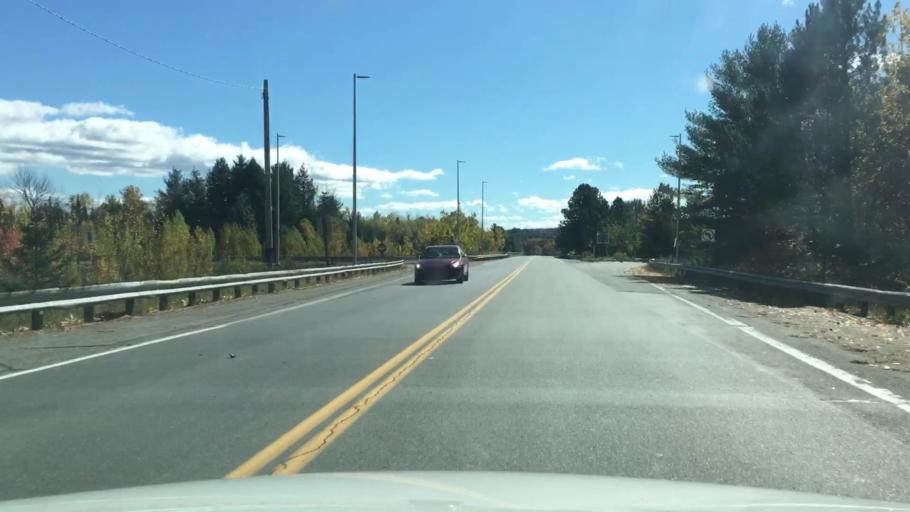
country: US
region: Maine
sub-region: Penobscot County
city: Medway
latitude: 45.6088
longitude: -68.5235
